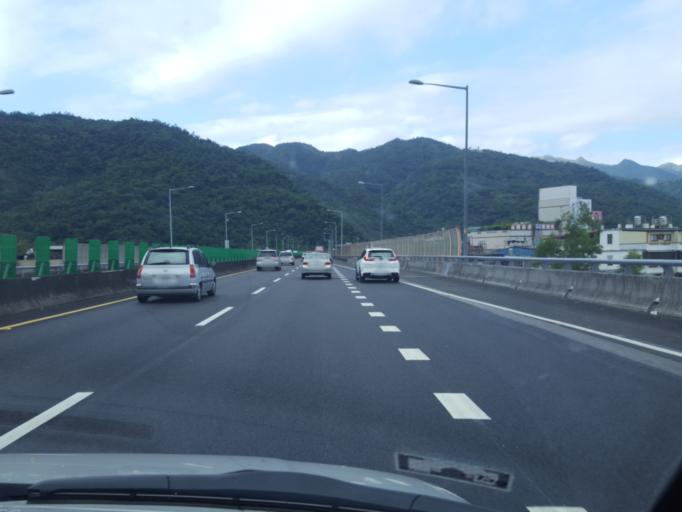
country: TW
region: Taiwan
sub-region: Yilan
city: Yilan
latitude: 24.8367
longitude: 121.7902
